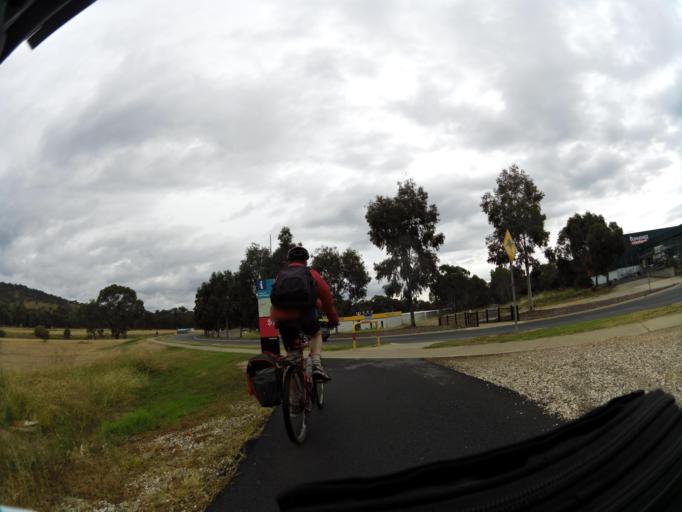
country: AU
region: Victoria
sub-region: Wodonga
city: Wodonga
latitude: -36.1384
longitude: 146.9070
